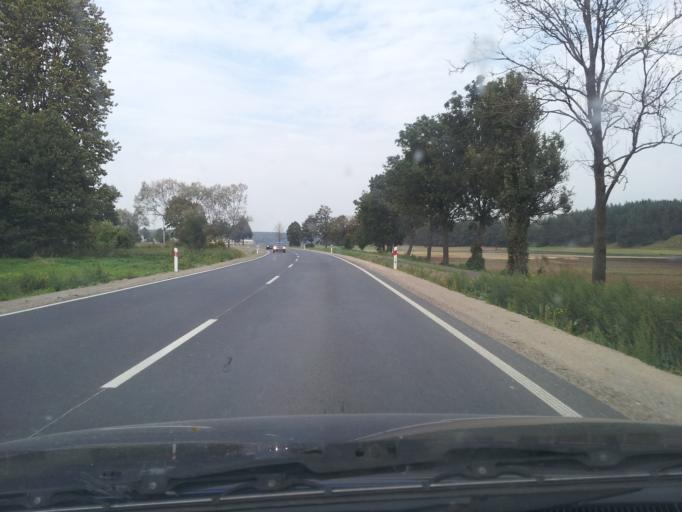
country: PL
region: Warmian-Masurian Voivodeship
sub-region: Powiat ilawski
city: Lubawa
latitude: 53.5099
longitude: 19.6747
